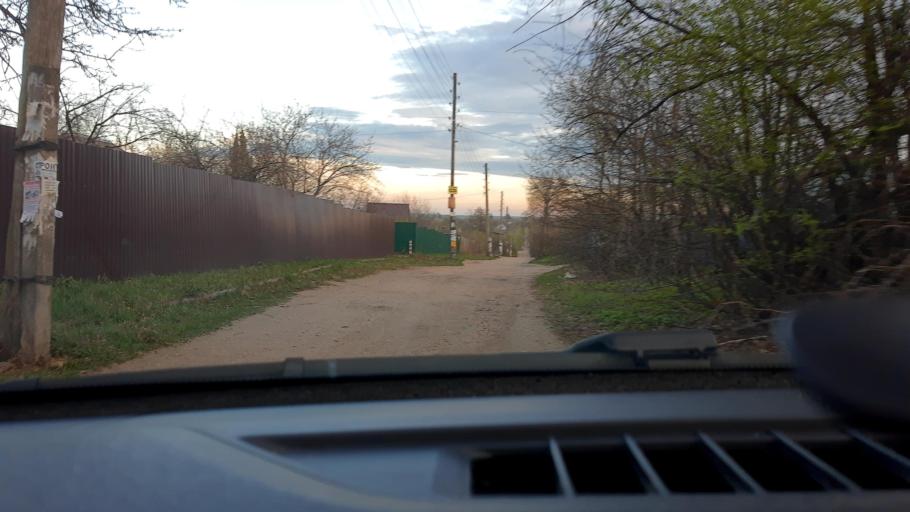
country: RU
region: Nizjnij Novgorod
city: Burevestnik
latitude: 56.1810
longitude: 43.7978
